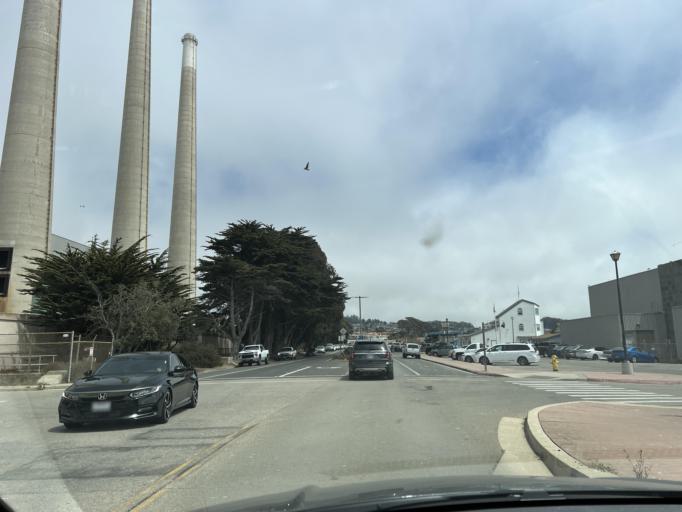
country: US
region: California
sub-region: San Luis Obispo County
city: Morro Bay
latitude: 35.3721
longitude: -120.8589
